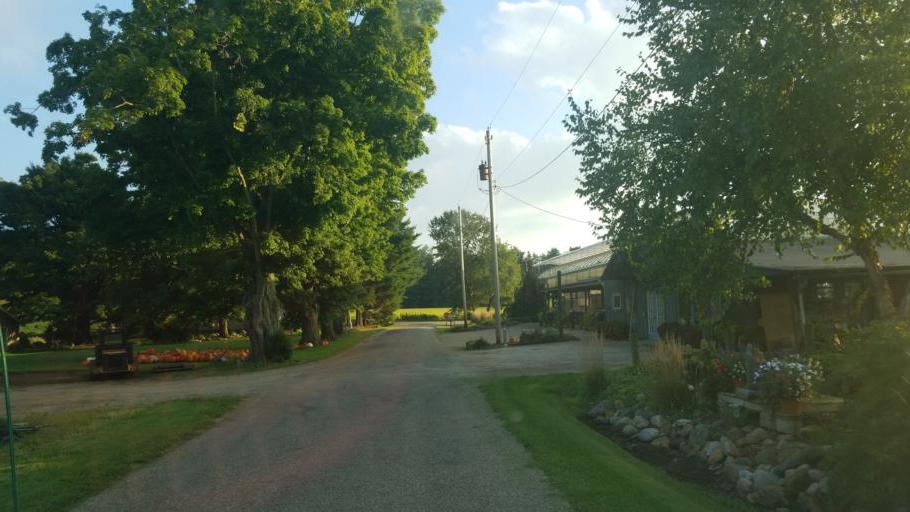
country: US
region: Ohio
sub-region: Ashland County
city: Loudonville
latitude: 40.6540
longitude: -82.1984
